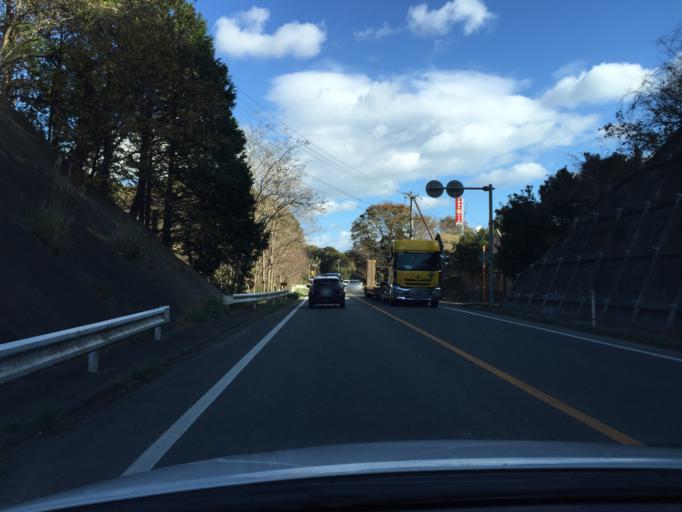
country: JP
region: Fukushima
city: Iwaki
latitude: 37.1888
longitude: 140.9975
